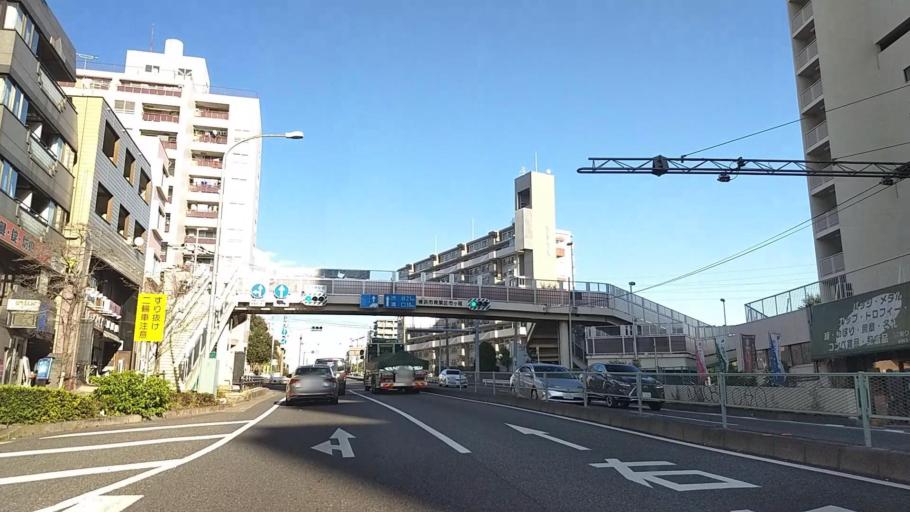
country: JP
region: Tokyo
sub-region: Machida-shi
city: Machida
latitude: 35.5523
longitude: 139.5405
